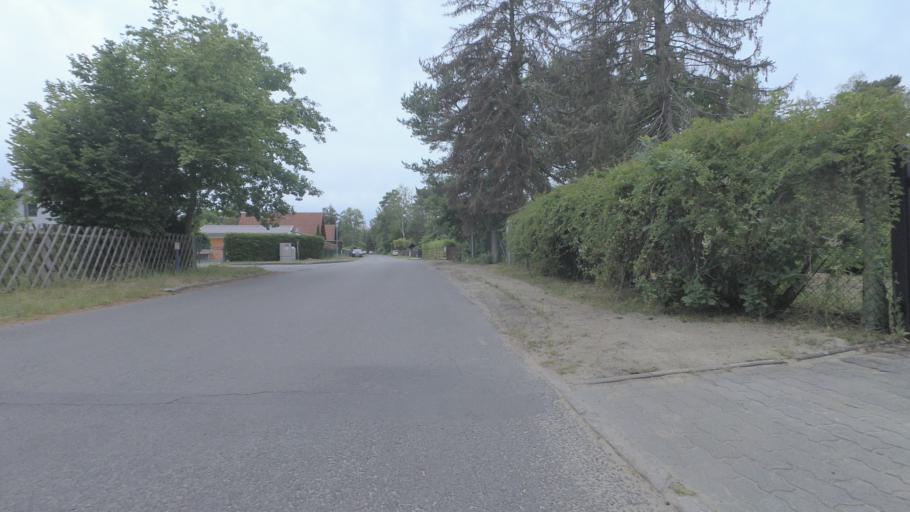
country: DE
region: Brandenburg
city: Bestensee
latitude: 52.2711
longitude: 13.7542
